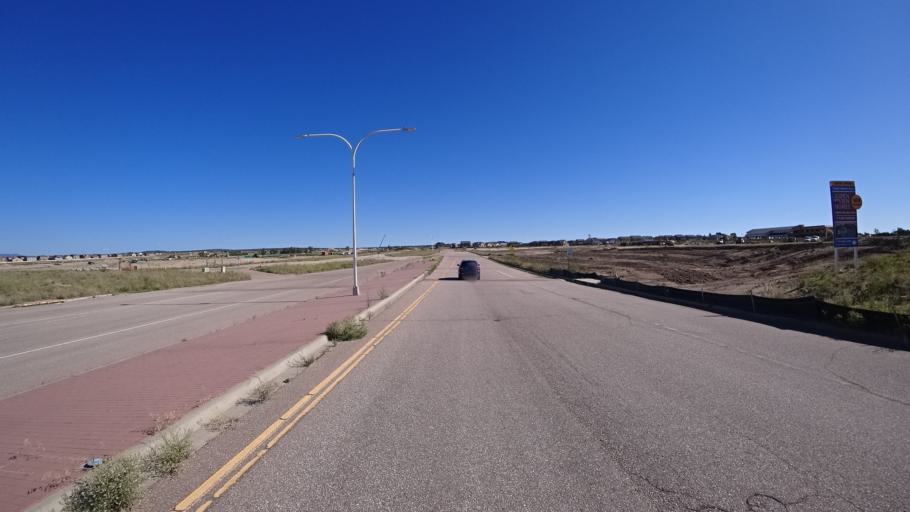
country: US
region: Colorado
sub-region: El Paso County
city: Black Forest
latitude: 38.9412
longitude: -104.6780
